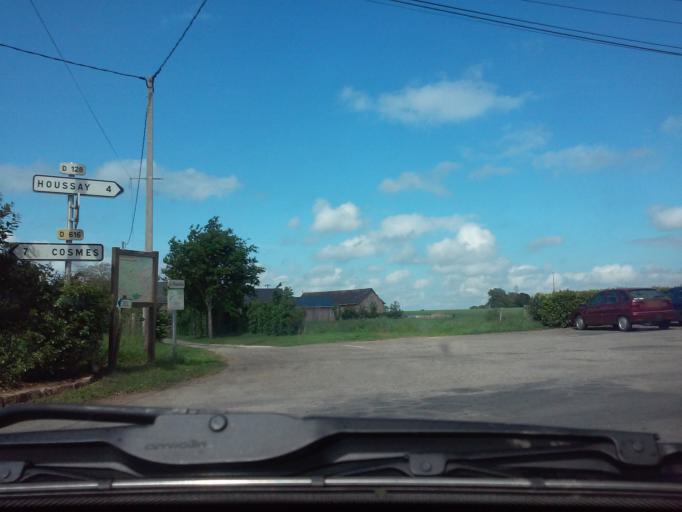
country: FR
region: Pays de la Loire
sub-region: Departement de la Mayenne
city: Quelaines-Saint-Gault
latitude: 47.9002
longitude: -0.7827
